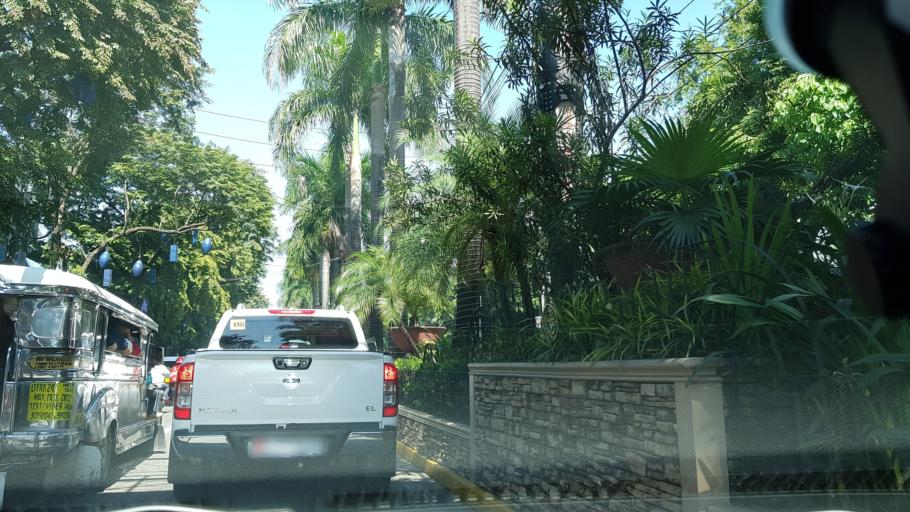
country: PH
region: Calabarzon
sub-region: Province of Rizal
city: Pateros
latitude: 14.5602
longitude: 121.0793
